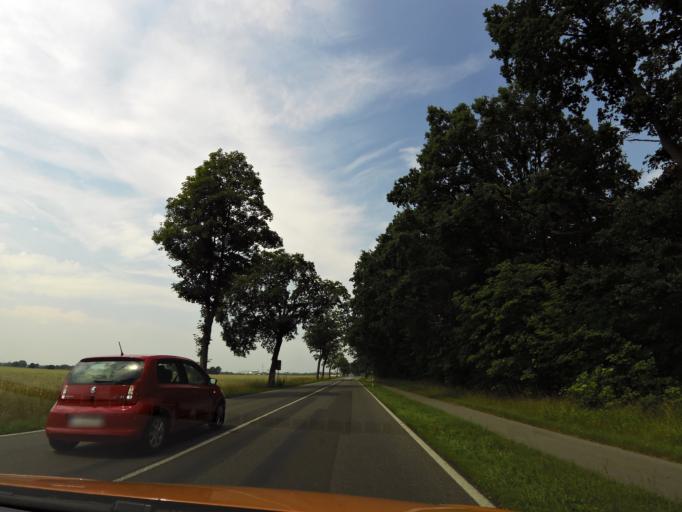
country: DE
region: Brandenburg
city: Kyritz
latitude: 52.9239
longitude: 12.4242
